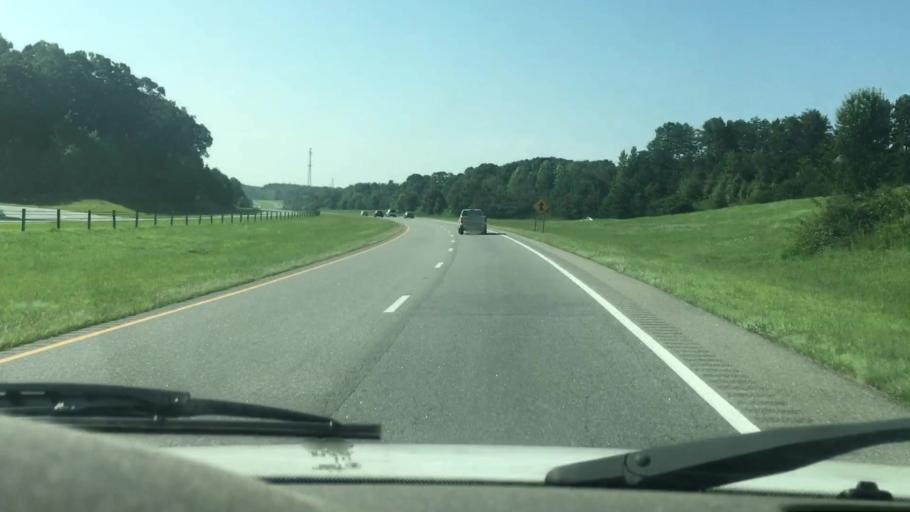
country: US
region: North Carolina
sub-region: Lincoln County
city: Lowesville
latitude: 35.3821
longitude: -81.0009
